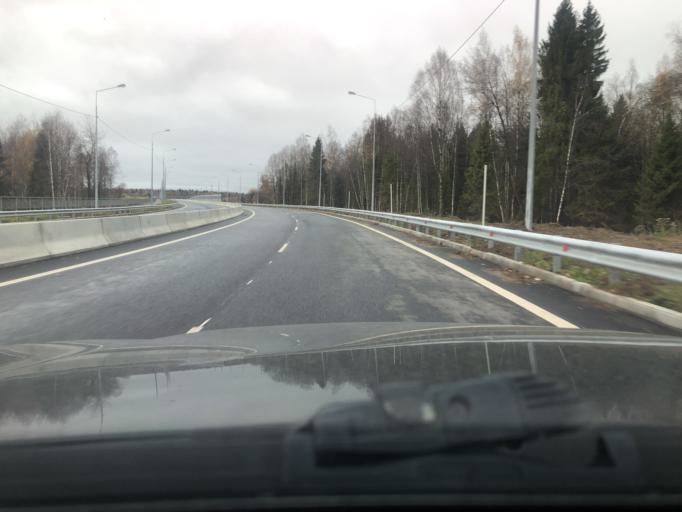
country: RU
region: Moskovskaya
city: Semkhoz
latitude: 56.3307
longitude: 38.0785
